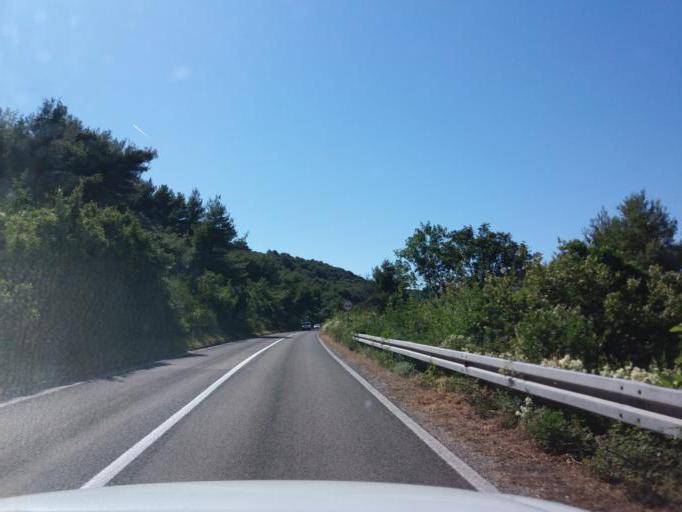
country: HR
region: Zadarska
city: Ugljan
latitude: 44.1089
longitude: 14.9314
